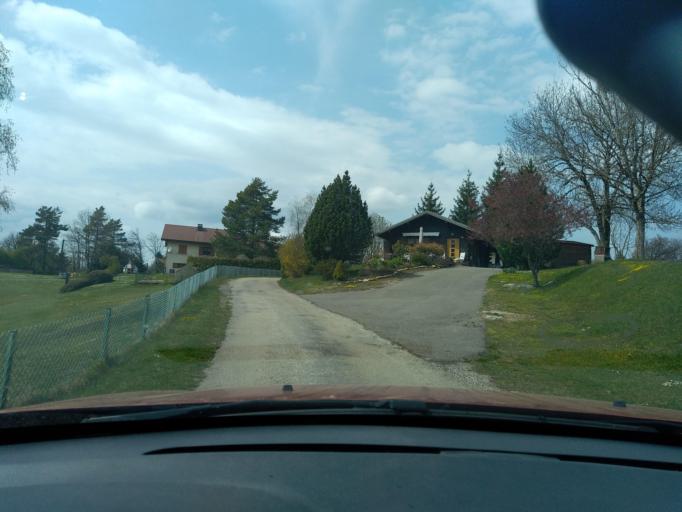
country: FR
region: Franche-Comte
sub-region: Departement du Jura
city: Moirans-en-Montagne
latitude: 46.4552
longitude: 5.7330
